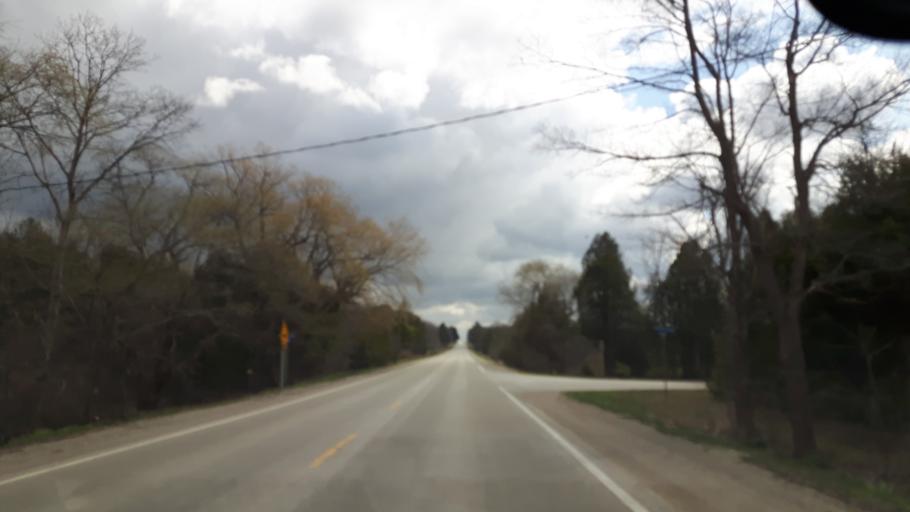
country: CA
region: Ontario
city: Bluewater
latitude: 43.5543
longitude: -81.6805
